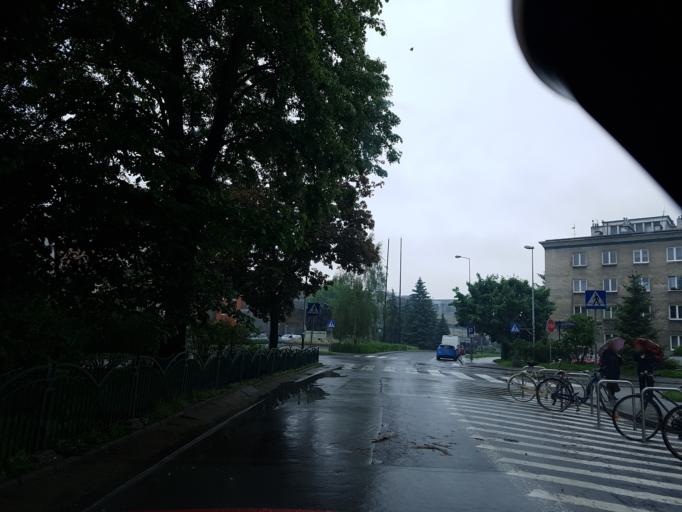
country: PL
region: Lesser Poland Voivodeship
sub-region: Krakow
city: Krakow
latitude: 50.0557
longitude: 19.9536
